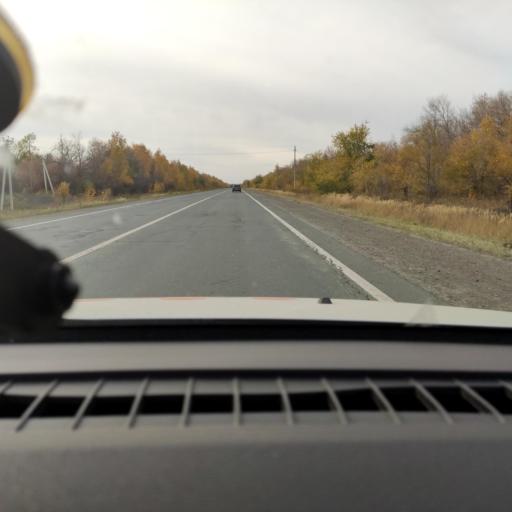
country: RU
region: Samara
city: Novokuybyshevsk
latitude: 52.9865
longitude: 49.8642
